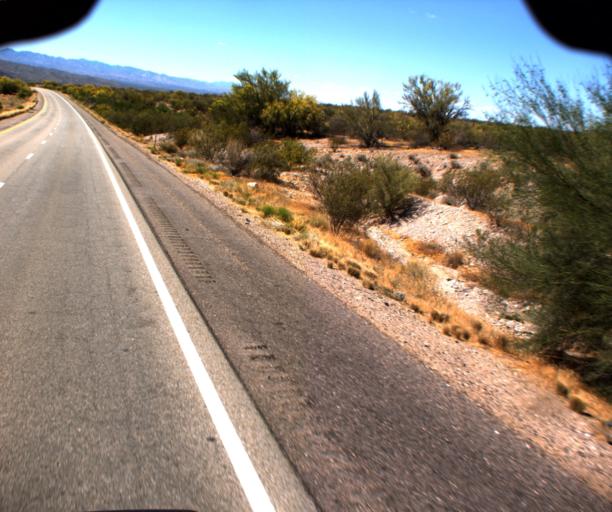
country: US
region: Arizona
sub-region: Yavapai County
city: Bagdad
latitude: 34.6258
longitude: -113.5361
